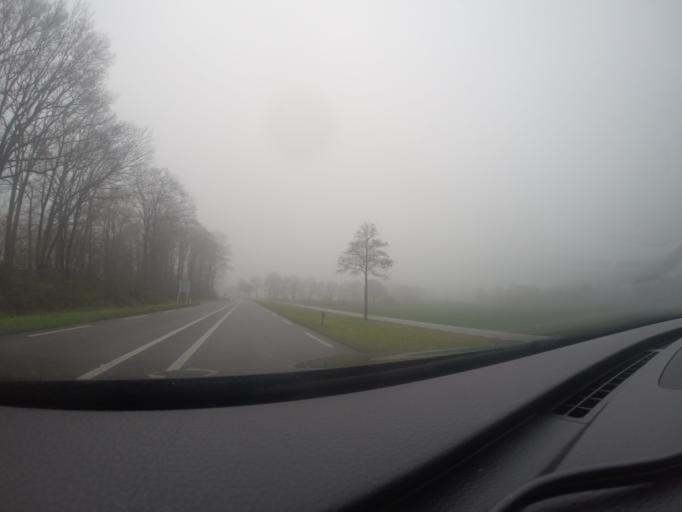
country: NL
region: Gelderland
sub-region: Gemeente Aalten
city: Aalten
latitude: 51.9017
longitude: 6.5850
